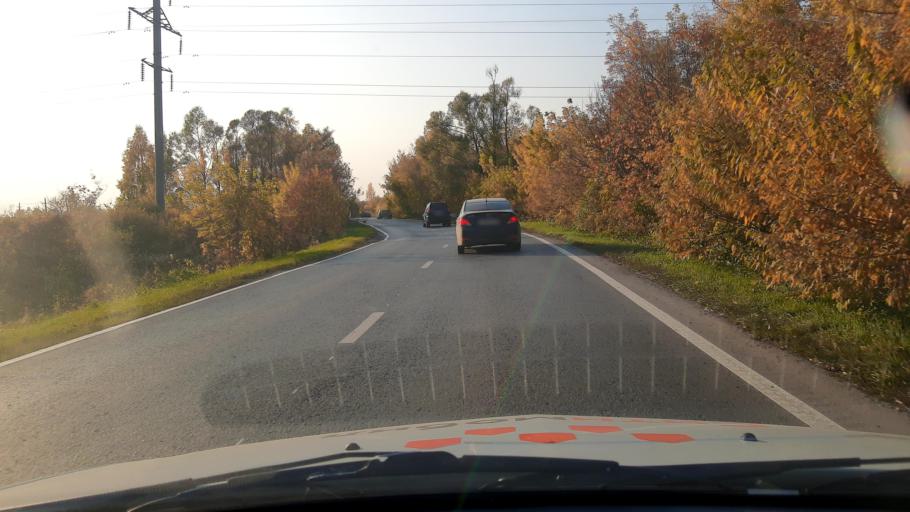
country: RU
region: Bashkortostan
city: Iglino
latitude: 54.7409
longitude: 56.2398
